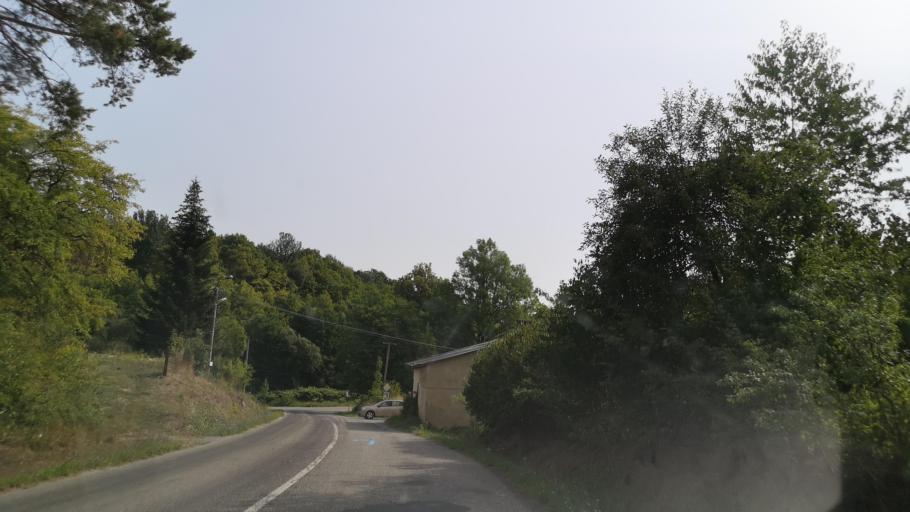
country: SK
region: Banskobystricky
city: Revuca
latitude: 48.5935
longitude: 20.0943
